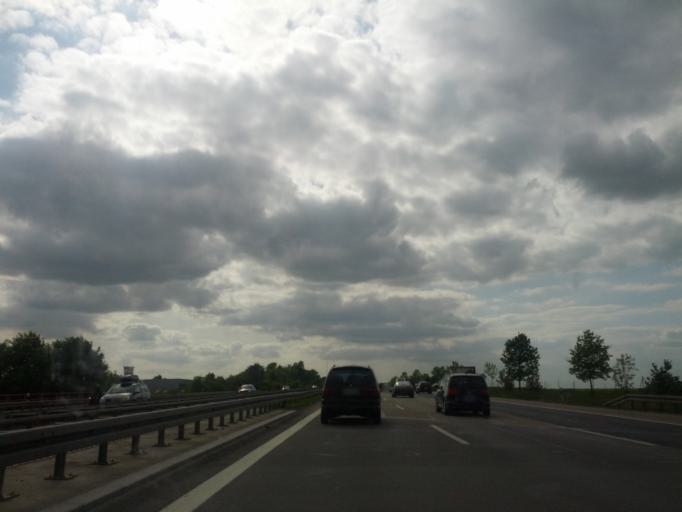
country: DE
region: Saxony
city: Wilsdruff
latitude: 51.0616
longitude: 13.5569
